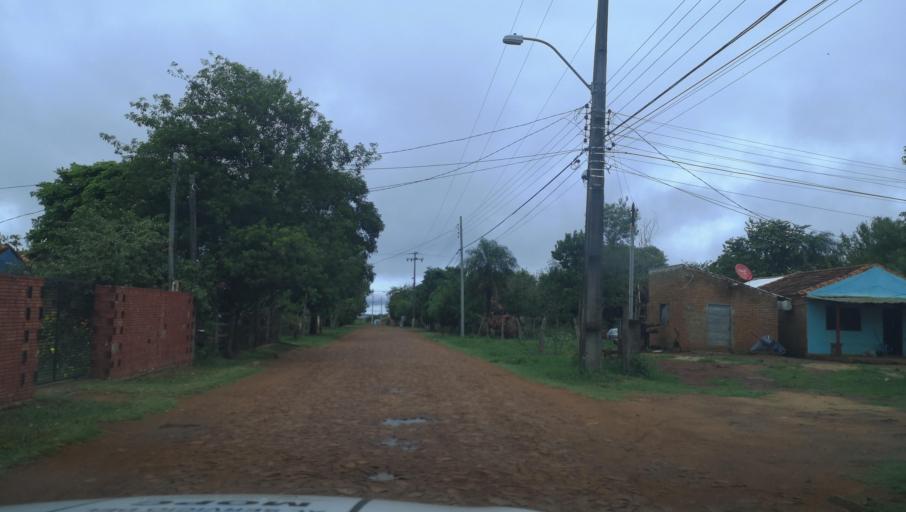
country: PY
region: Misiones
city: Santa Maria
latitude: -26.9003
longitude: -57.0369
